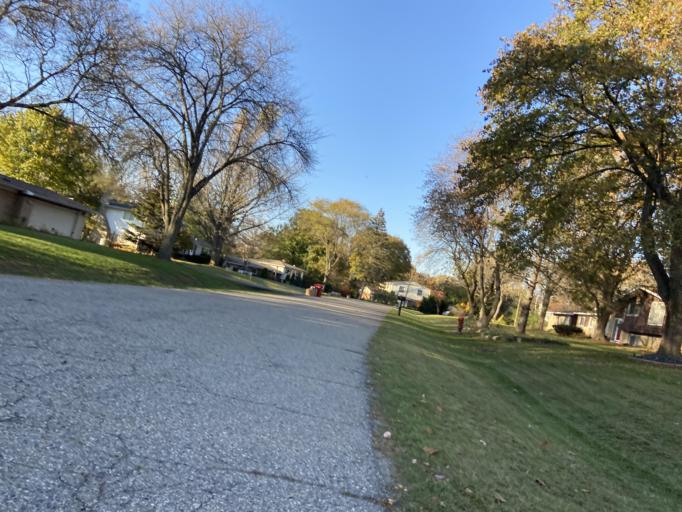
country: US
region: Michigan
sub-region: Oakland County
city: Franklin
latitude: 42.5299
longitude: -83.3386
